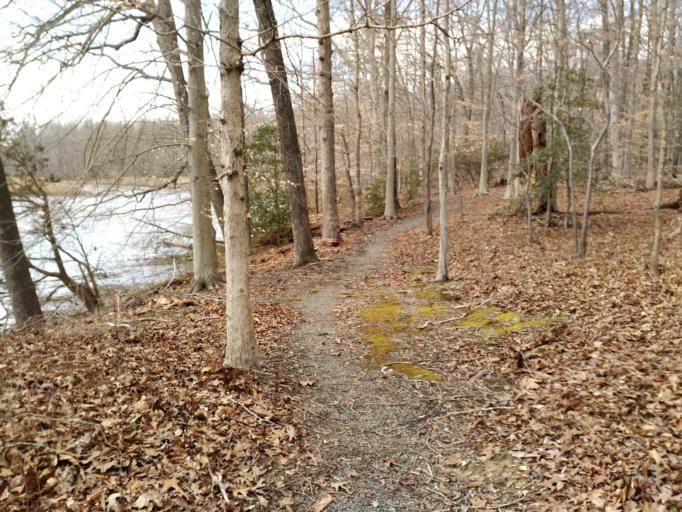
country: US
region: Maryland
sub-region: Anne Arundel County
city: Mayo
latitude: 38.8827
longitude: -76.5532
